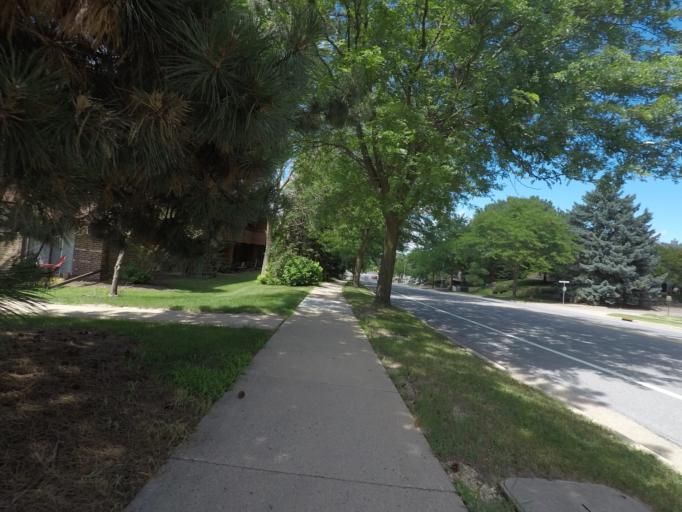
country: US
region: Wisconsin
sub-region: Dane County
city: Middleton
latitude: 43.0587
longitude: -89.5178
